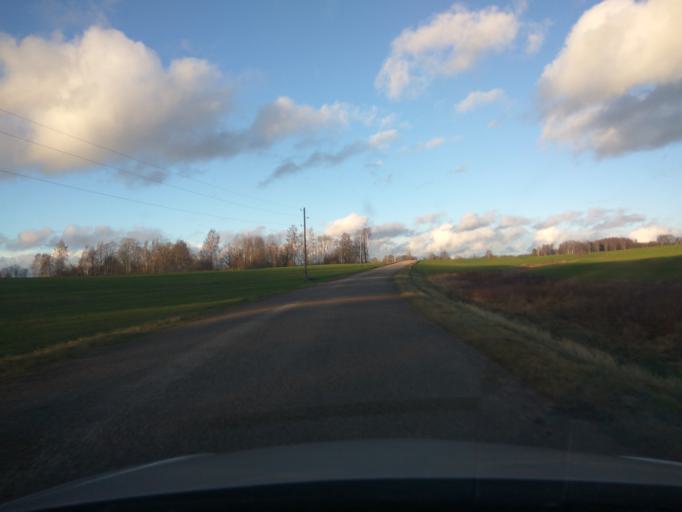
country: LV
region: Aizpute
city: Aizpute
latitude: 56.7623
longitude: 21.7815
